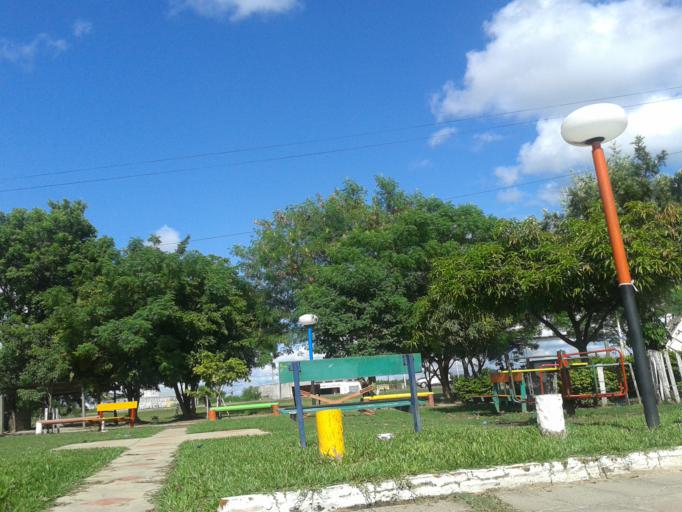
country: AR
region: Formosa
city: Clorinda
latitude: -25.2833
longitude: -57.7345
